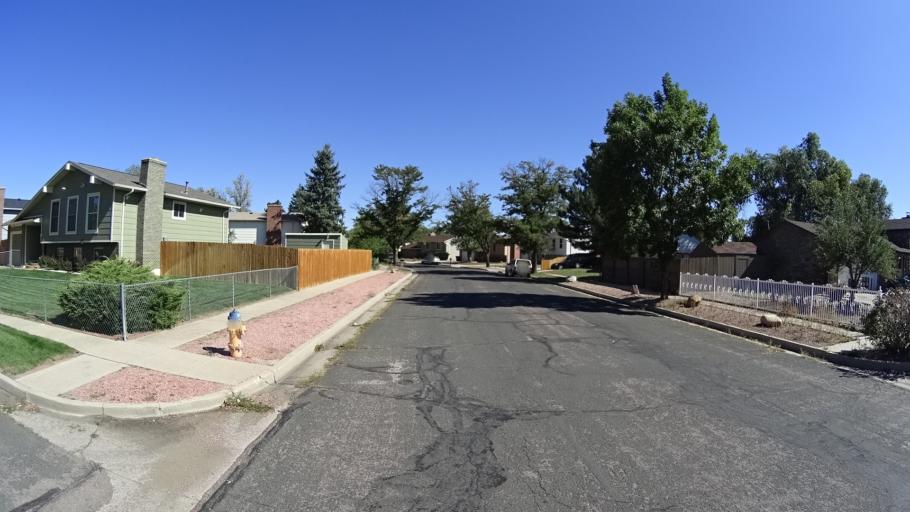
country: US
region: Colorado
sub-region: El Paso County
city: Stratmoor
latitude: 38.7925
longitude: -104.7459
